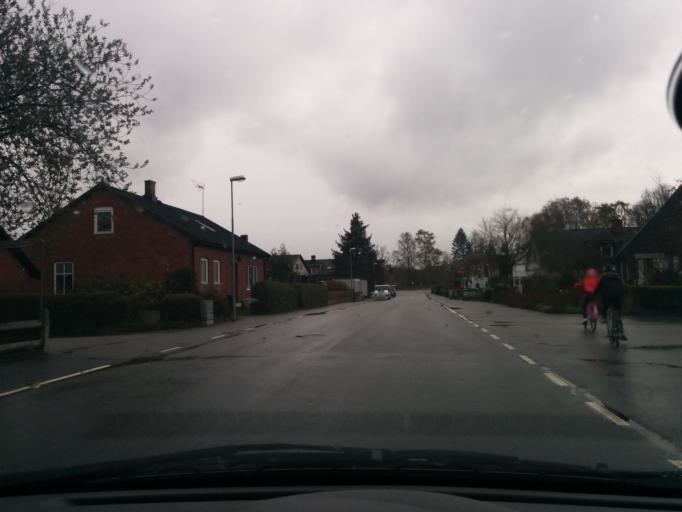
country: SE
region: Skane
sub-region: Lunds Kommun
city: Genarp
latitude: 55.6019
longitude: 13.3961
